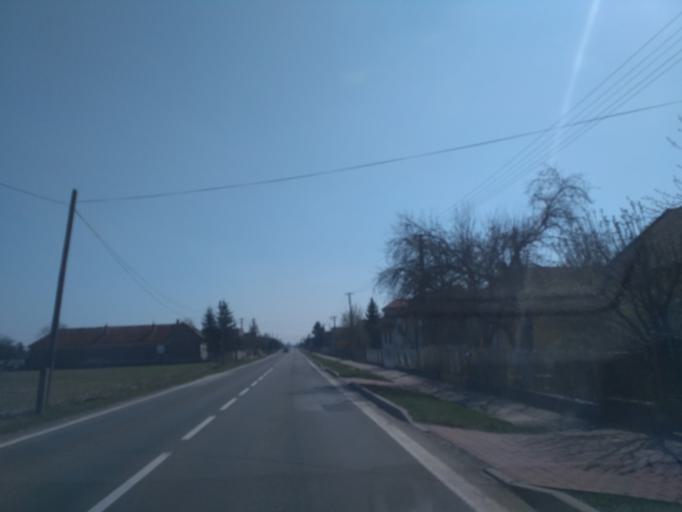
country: SK
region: Kosicky
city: Secovce
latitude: 48.7331
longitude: 21.7014
